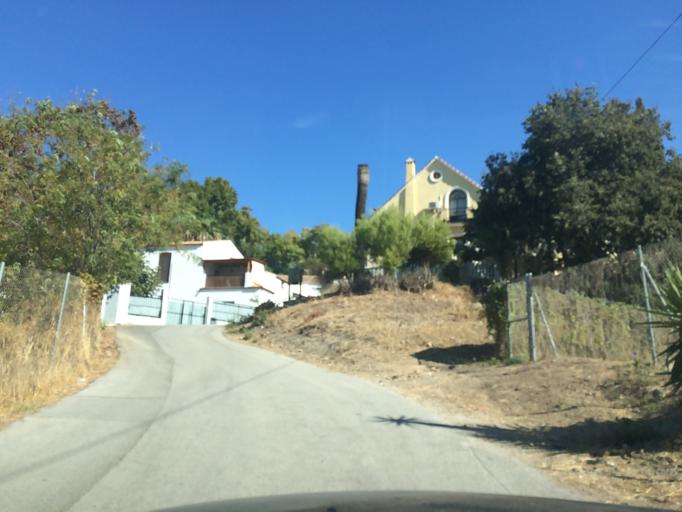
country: ES
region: Andalusia
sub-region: Provincia de Malaga
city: Malaga
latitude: 36.7627
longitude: -4.4217
